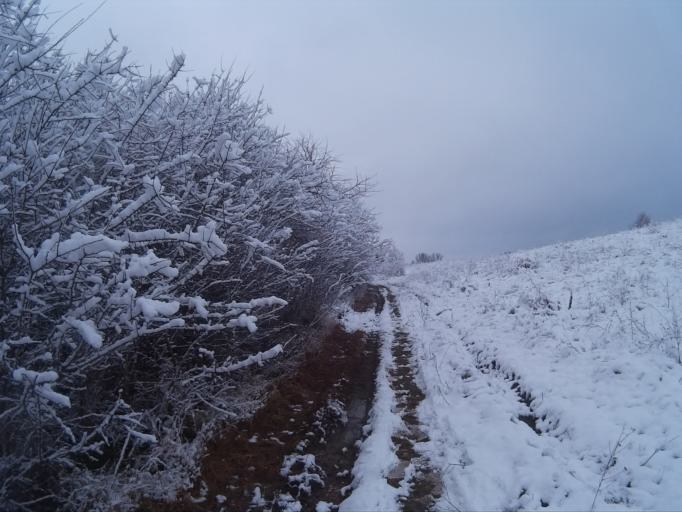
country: HU
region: Fejer
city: Szarliget
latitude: 47.5339
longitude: 18.5387
